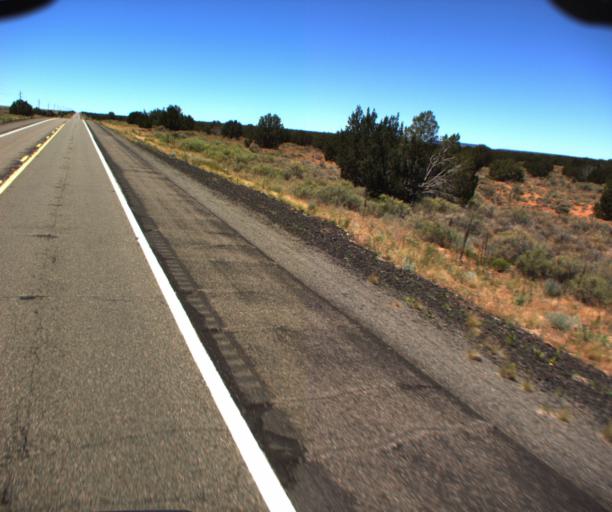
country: US
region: Arizona
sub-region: Coconino County
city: LeChee
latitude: 34.8202
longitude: -110.9622
